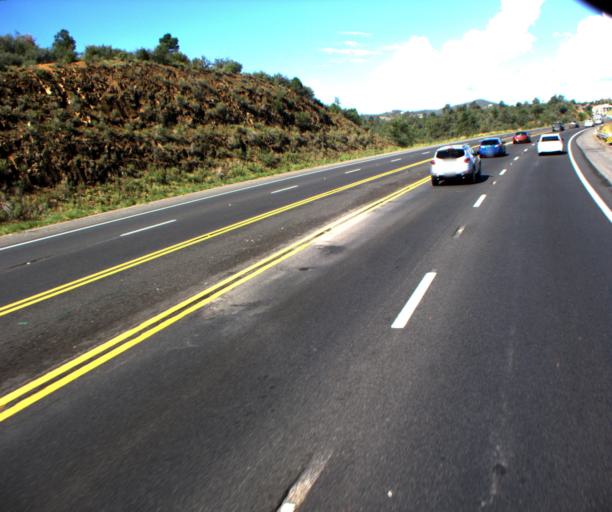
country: US
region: Arizona
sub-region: Yavapai County
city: Prescott
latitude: 34.5493
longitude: -112.3899
